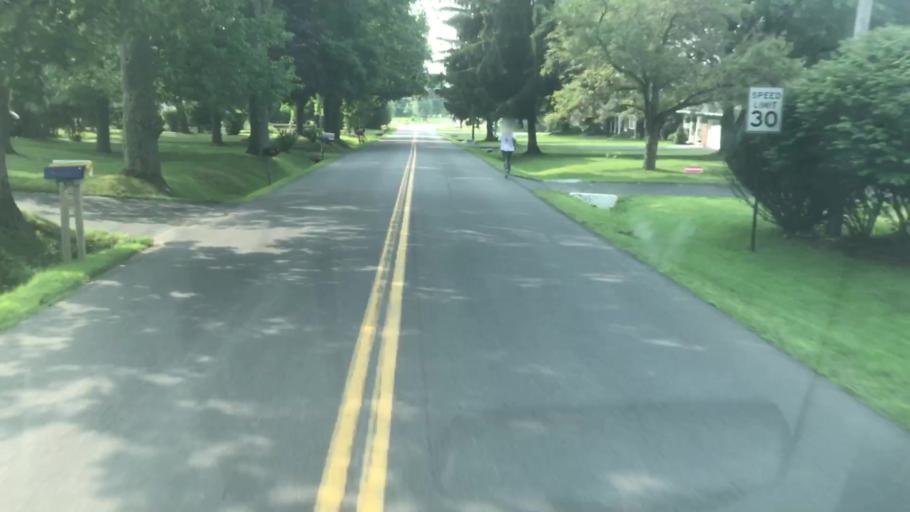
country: US
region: New York
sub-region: Cayuga County
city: Melrose Park
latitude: 42.9138
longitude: -76.5298
